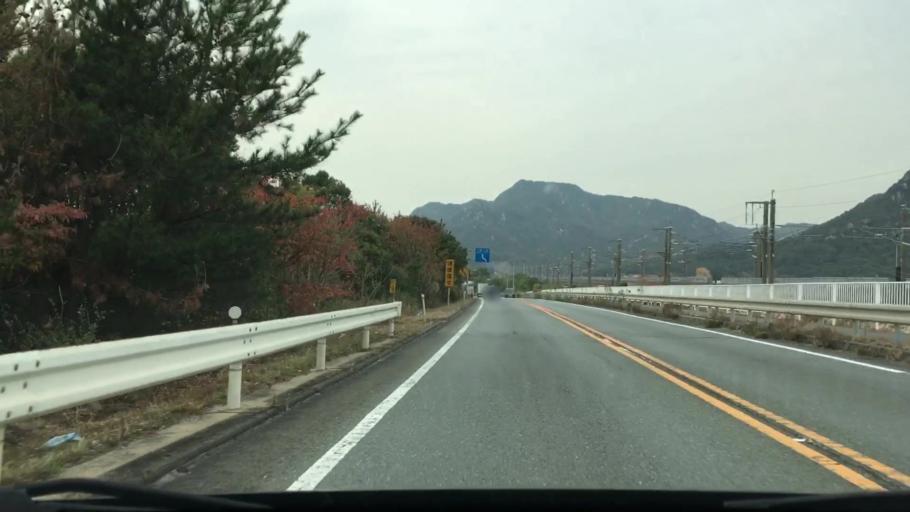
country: JP
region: Yamaguchi
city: Hofu
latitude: 34.0743
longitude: 131.5721
